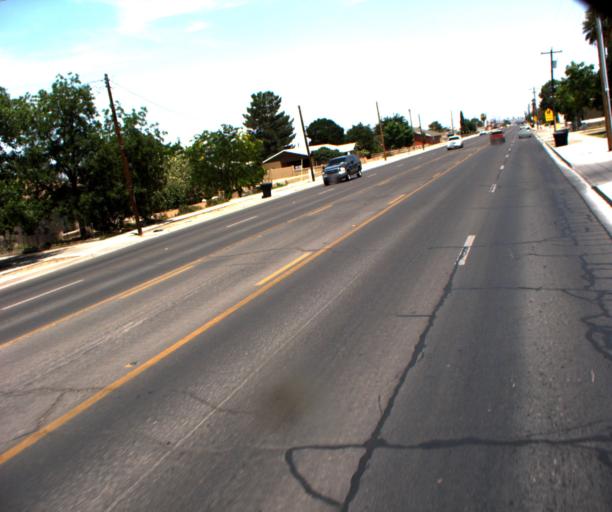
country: US
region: Arizona
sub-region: Graham County
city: Thatcher
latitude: 32.8491
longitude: -109.7608
